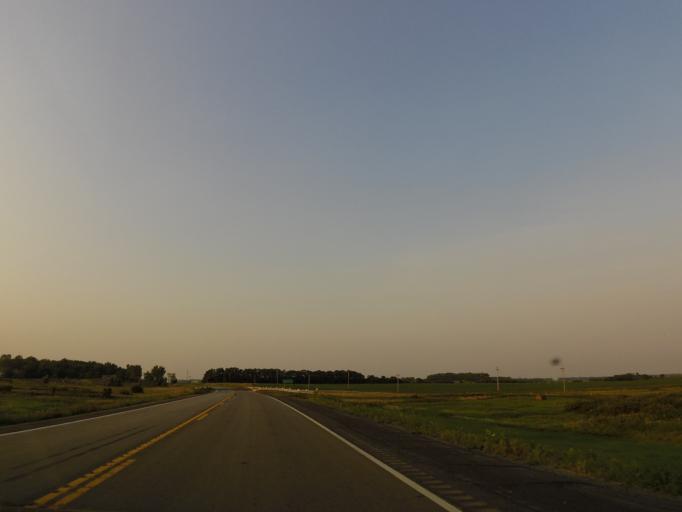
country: US
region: North Dakota
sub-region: Grand Forks County
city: Larimore
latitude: 47.7458
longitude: -97.6250
